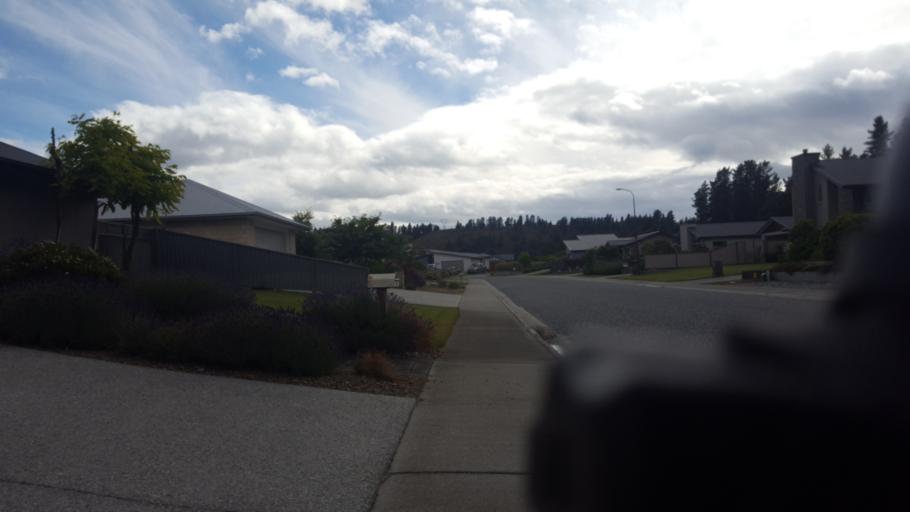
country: NZ
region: Otago
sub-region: Queenstown-Lakes District
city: Wanaka
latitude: -45.2407
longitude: 169.3810
